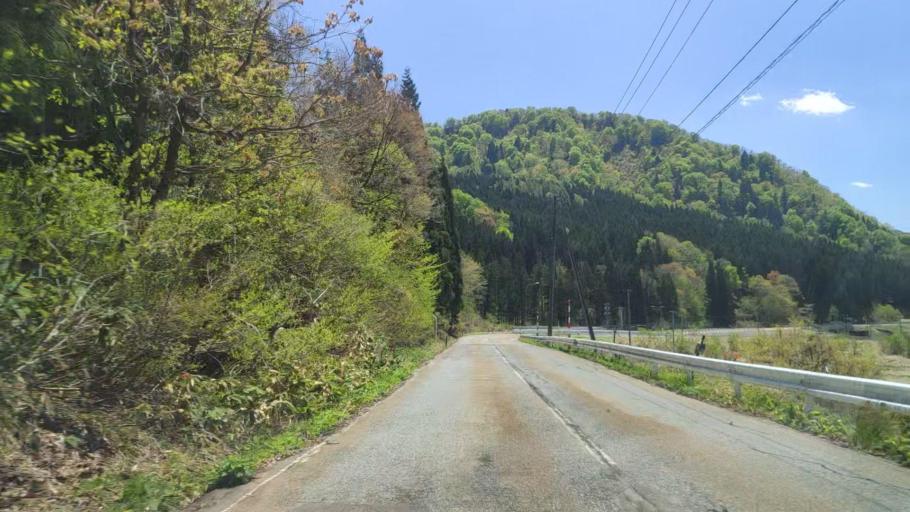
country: JP
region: Yamagata
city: Shinjo
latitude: 38.9548
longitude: 140.3584
